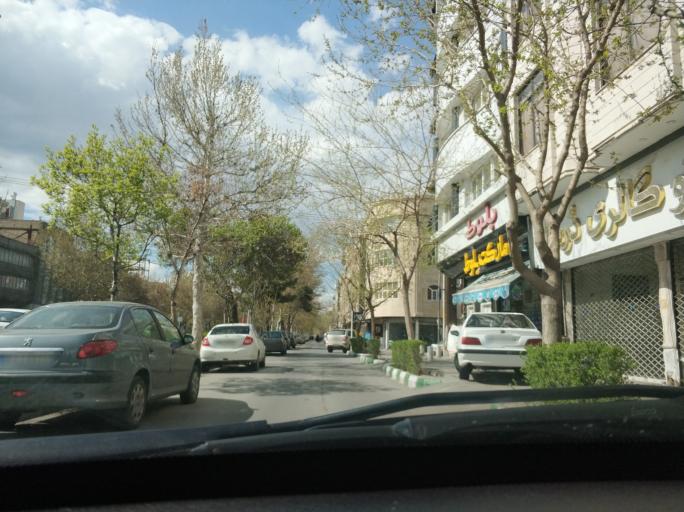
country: IR
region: Razavi Khorasan
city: Mashhad
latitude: 36.2694
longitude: 59.5976
